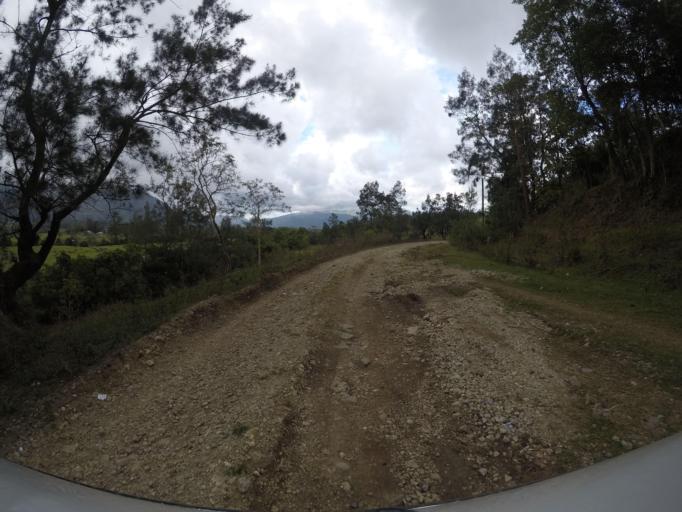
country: TL
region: Baucau
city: Venilale
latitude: -8.6718
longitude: 126.6309
